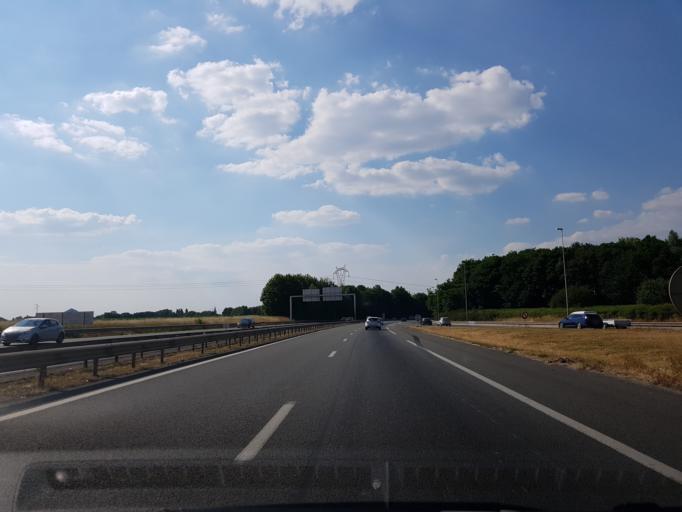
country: FR
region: Nord-Pas-de-Calais
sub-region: Departement du Nord
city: Auby
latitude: 50.4106
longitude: 3.0352
